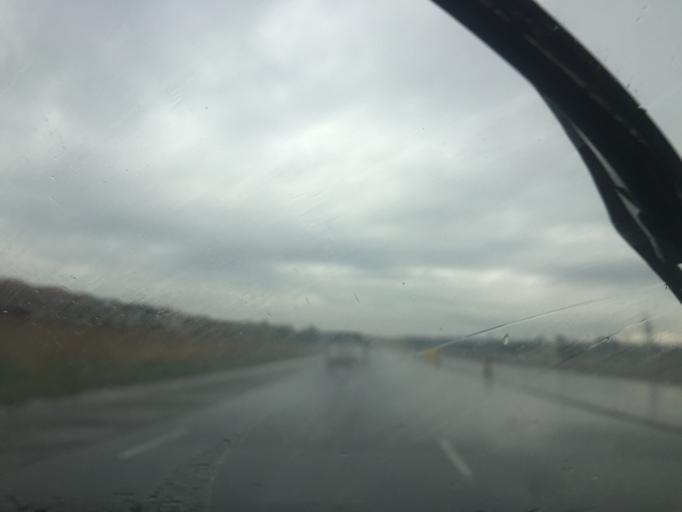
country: ZA
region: Gauteng
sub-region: City of Tshwane Metropolitan Municipality
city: Centurion
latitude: -25.8910
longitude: 28.1171
